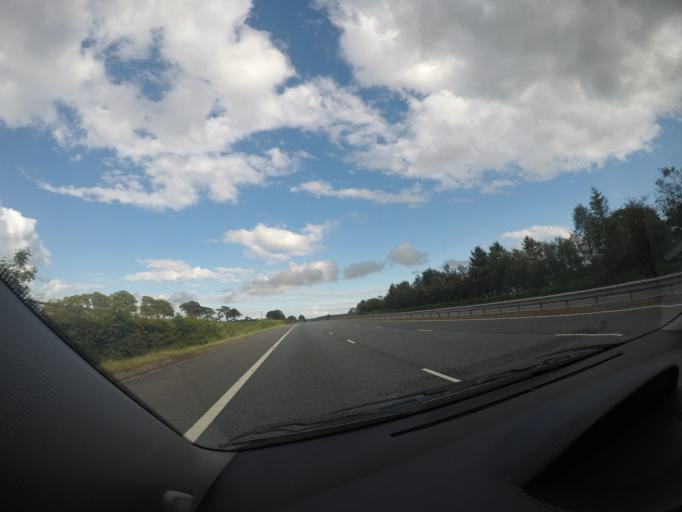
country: GB
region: Scotland
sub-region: Dumfries and Galloway
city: Lockerbie
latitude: 55.0720
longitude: -3.2965
